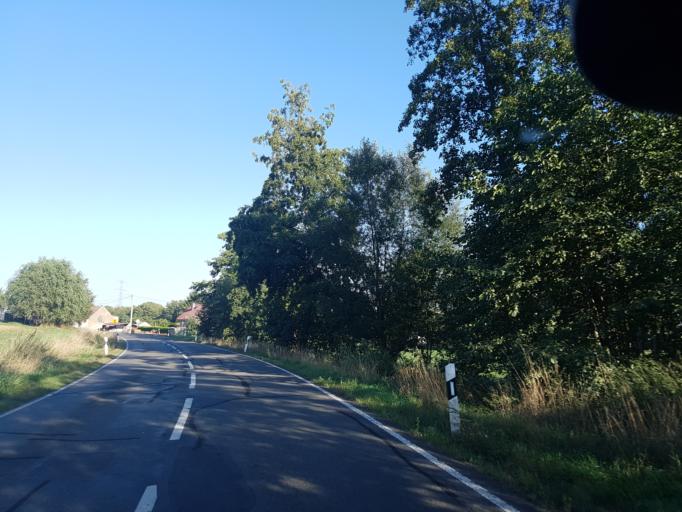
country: DE
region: Saxony
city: Ostrau
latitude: 51.1946
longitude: 13.1397
